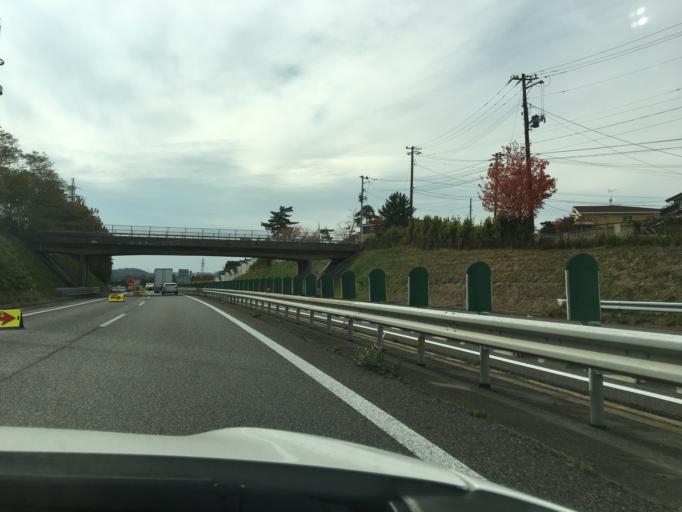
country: JP
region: Fukushima
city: Koriyama
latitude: 37.4283
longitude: 140.3370
